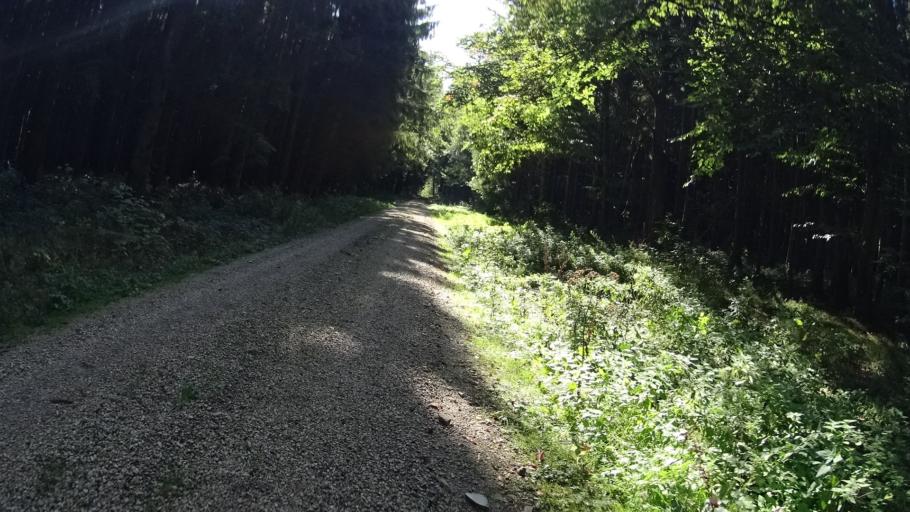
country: DE
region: Bavaria
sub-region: Upper Bavaria
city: Hitzhofen
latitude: 48.8811
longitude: 11.3063
